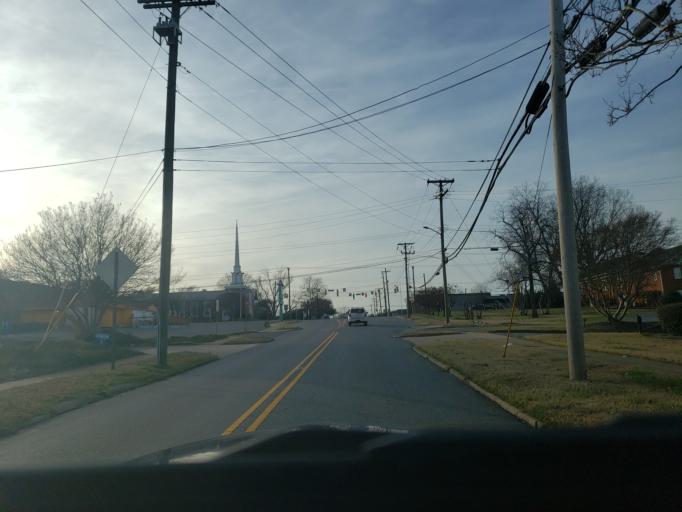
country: US
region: North Carolina
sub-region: Cleveland County
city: Shelby
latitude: 35.2893
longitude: -81.5360
